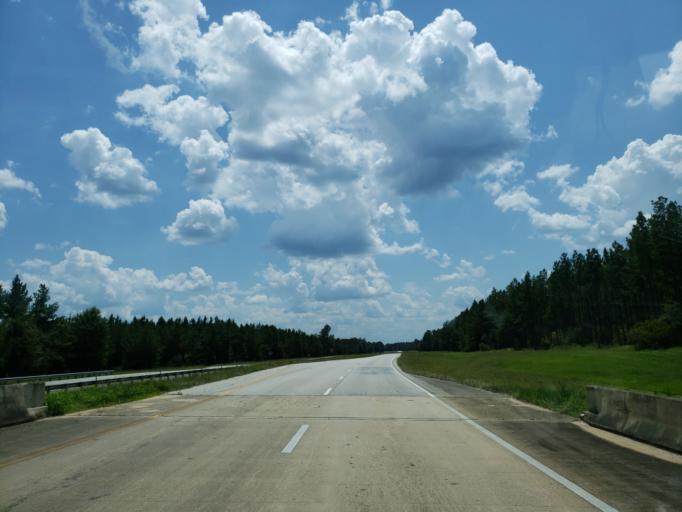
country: US
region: Mississippi
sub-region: Greene County
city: Leakesville
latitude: 31.2830
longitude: -88.5054
